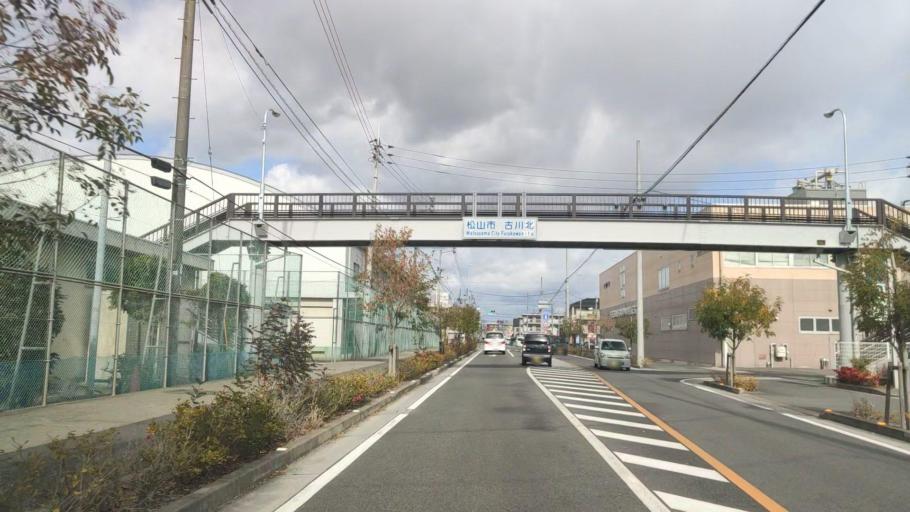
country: JP
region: Ehime
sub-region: Shikoku-chuo Shi
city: Matsuyama
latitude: 33.8108
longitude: 132.7608
